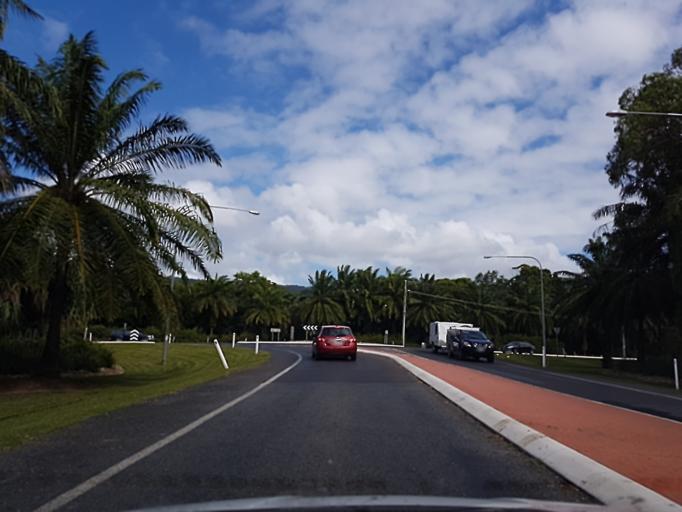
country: AU
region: Queensland
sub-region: Cairns
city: Port Douglas
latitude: -16.5280
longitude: 145.4621
